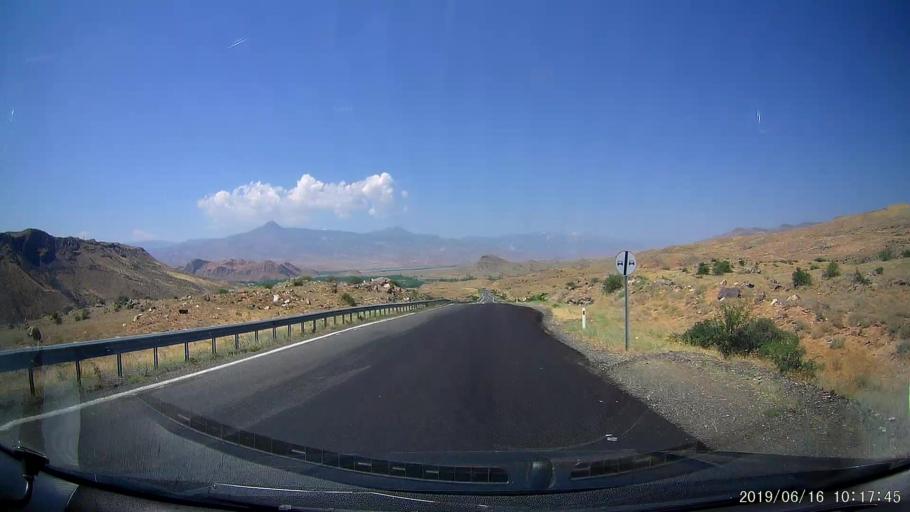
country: TR
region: Igdir
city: Tuzluca
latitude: 40.1644
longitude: 43.6771
